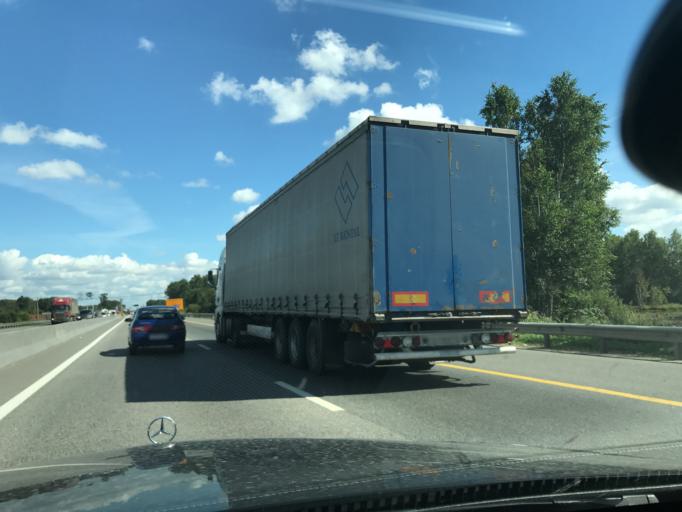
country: RU
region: Nizjnij Novgorod
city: Babino
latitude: 56.3056
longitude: 43.6555
